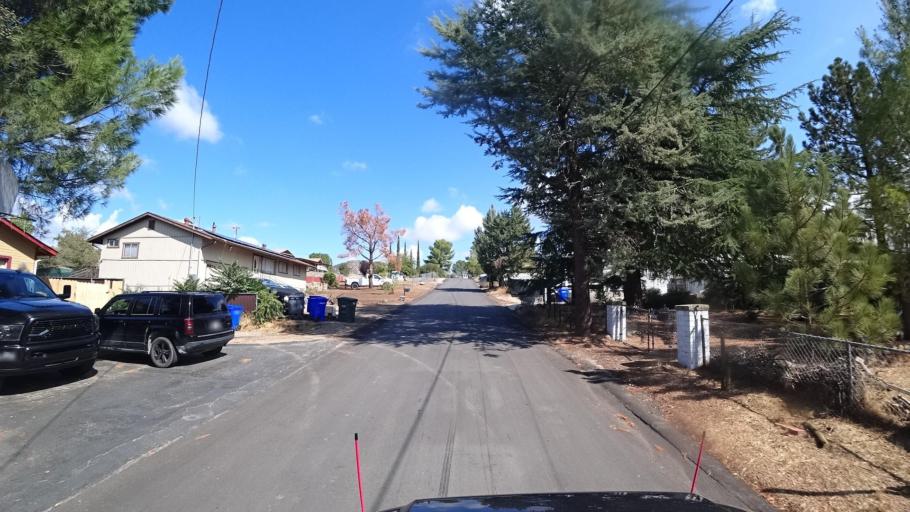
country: US
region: California
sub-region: San Diego County
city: Campo
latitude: 32.6790
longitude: -116.5011
